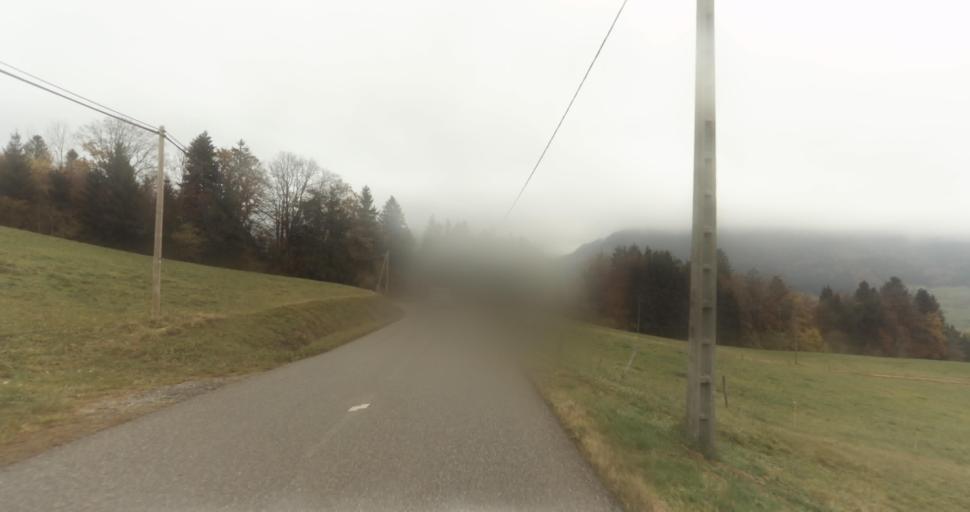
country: FR
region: Rhone-Alpes
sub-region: Departement de la Haute-Savoie
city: Thorens-Glieres
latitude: 46.0046
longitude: 6.2401
